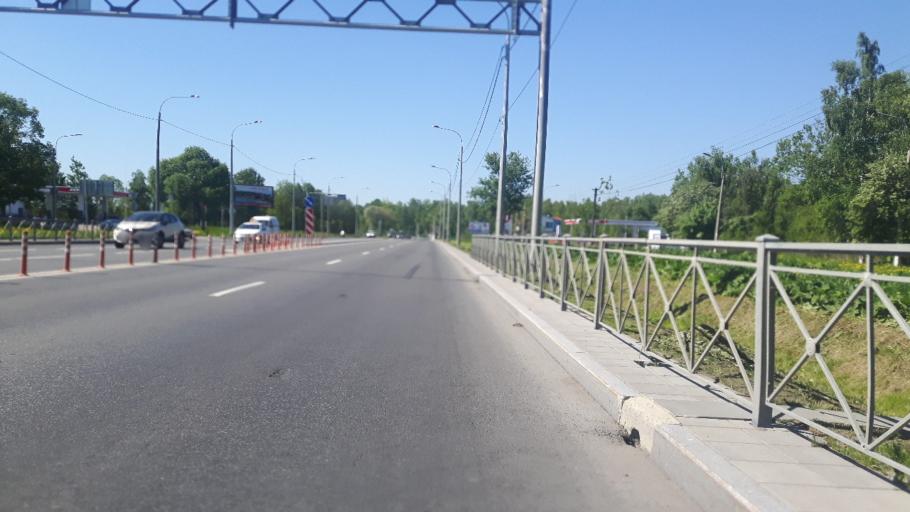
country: RU
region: Leningrad
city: Gorbunki
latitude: 59.8692
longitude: 29.9739
